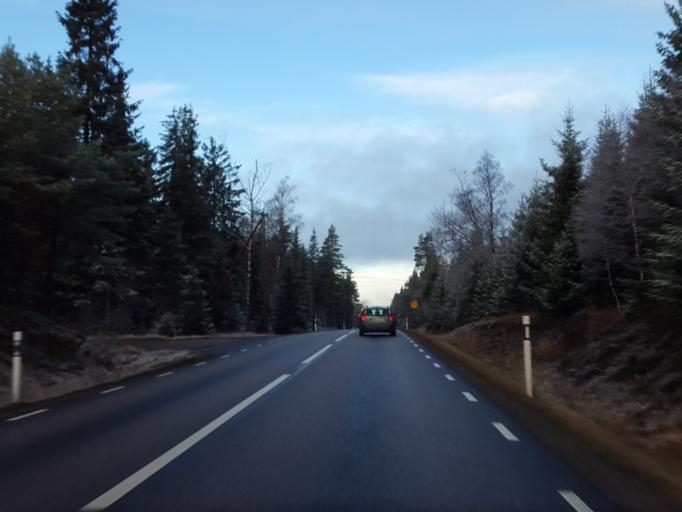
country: SE
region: Vaestra Goetaland
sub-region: Boras Kommun
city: Sjomarken
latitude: 57.7565
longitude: 12.8505
